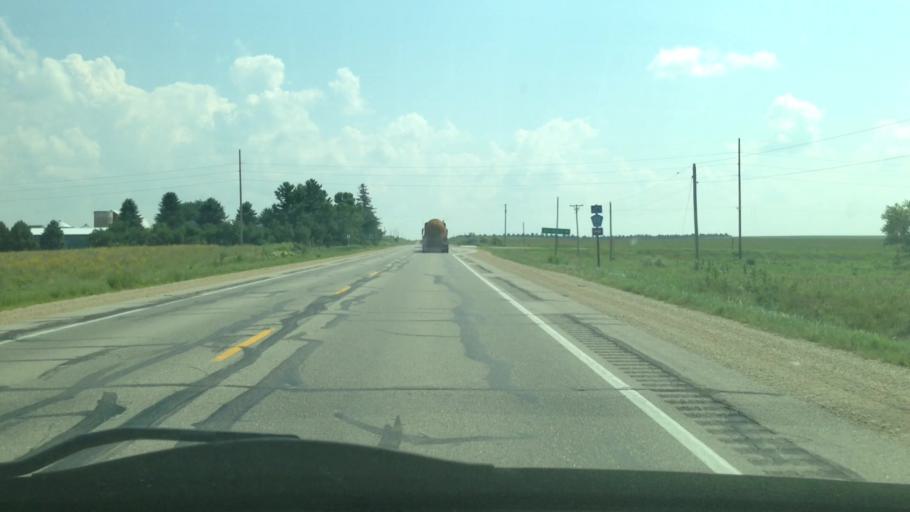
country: US
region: Iowa
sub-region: Chickasaw County
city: New Hampton
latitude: 43.2007
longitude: -92.2983
